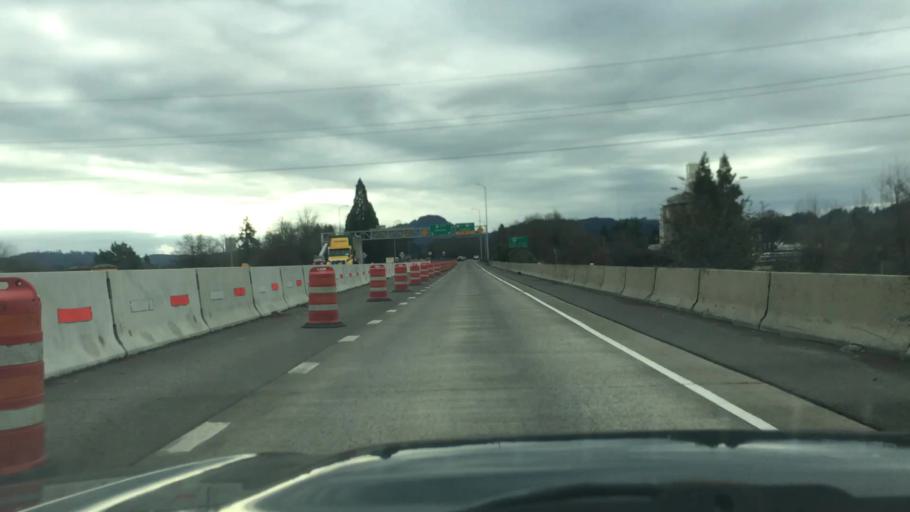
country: US
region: Oregon
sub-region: Lane County
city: Eugene
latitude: 44.0603
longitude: -123.1013
